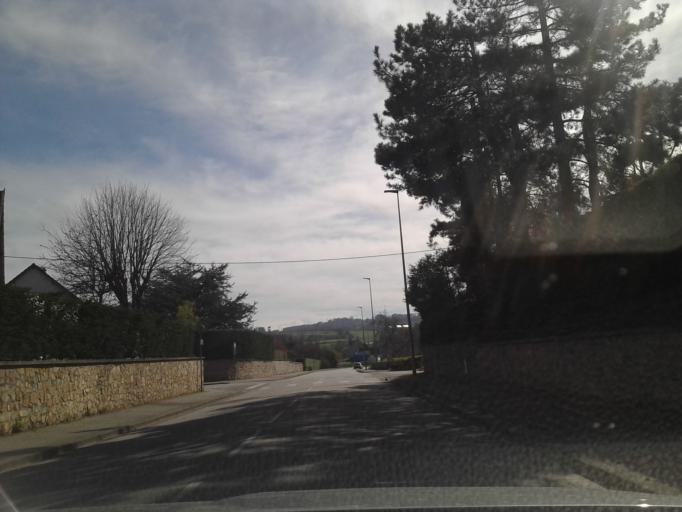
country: FR
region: Lower Normandy
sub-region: Departement de la Manche
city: Tourlaville
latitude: 49.6394
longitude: -1.5733
